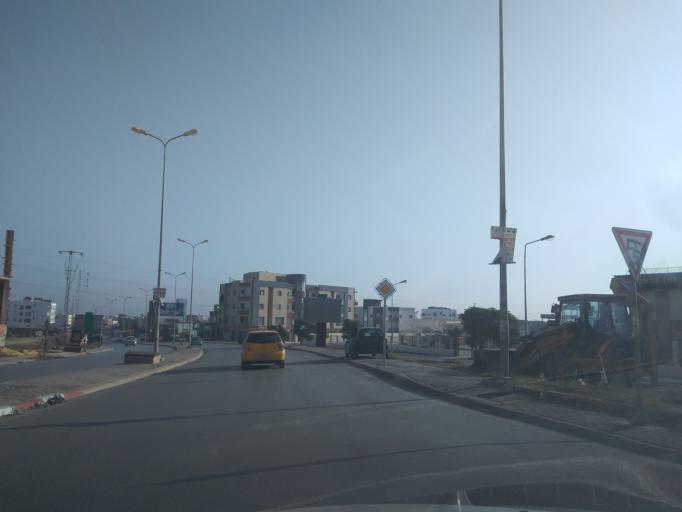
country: TN
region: Manouba
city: Manouba
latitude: 36.7857
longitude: 10.0811
